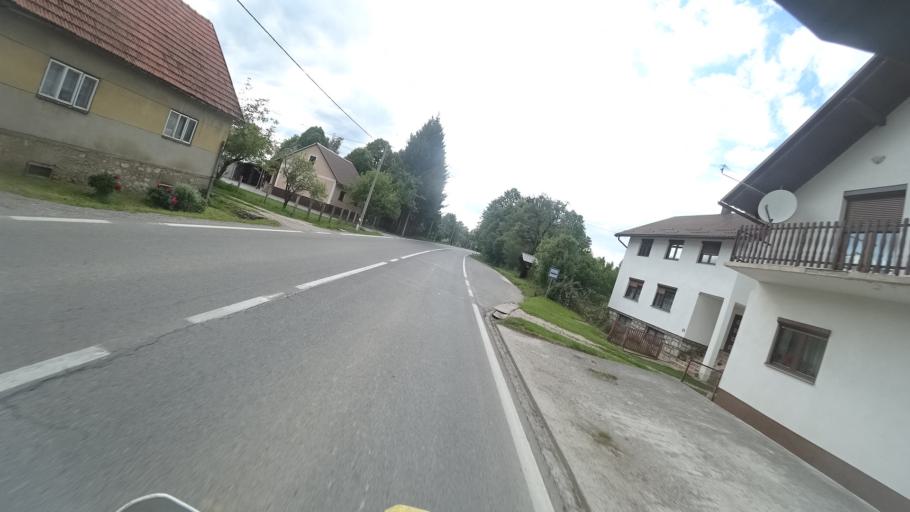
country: HR
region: Licko-Senjska
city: Gospic
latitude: 44.5154
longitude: 15.4211
